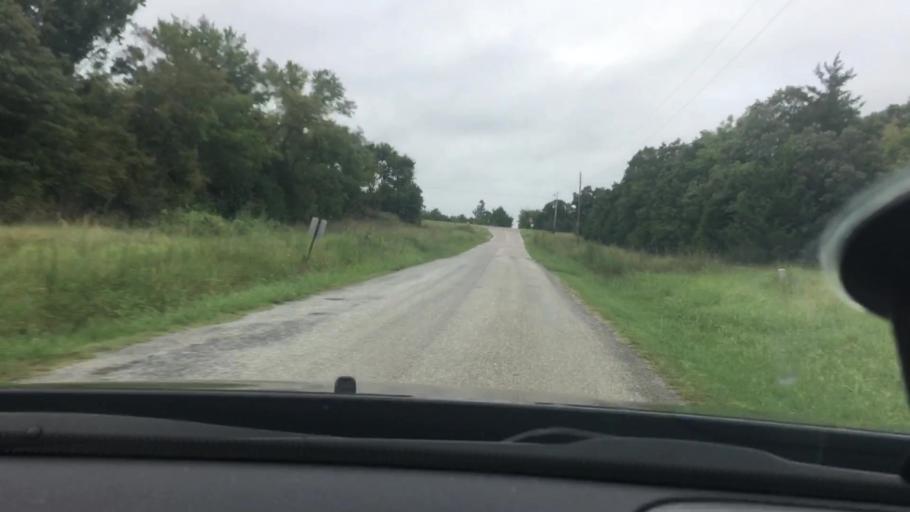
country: US
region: Oklahoma
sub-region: Pontotoc County
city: Byng
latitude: 34.8003
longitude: -96.5475
